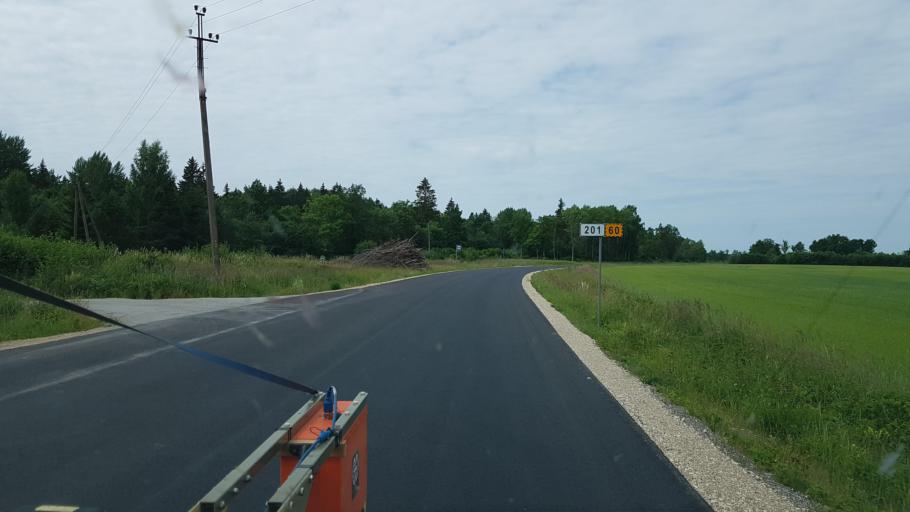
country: EE
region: Paernumaa
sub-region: Halinga vald
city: Parnu-Jaagupi
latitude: 58.6236
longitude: 24.3651
